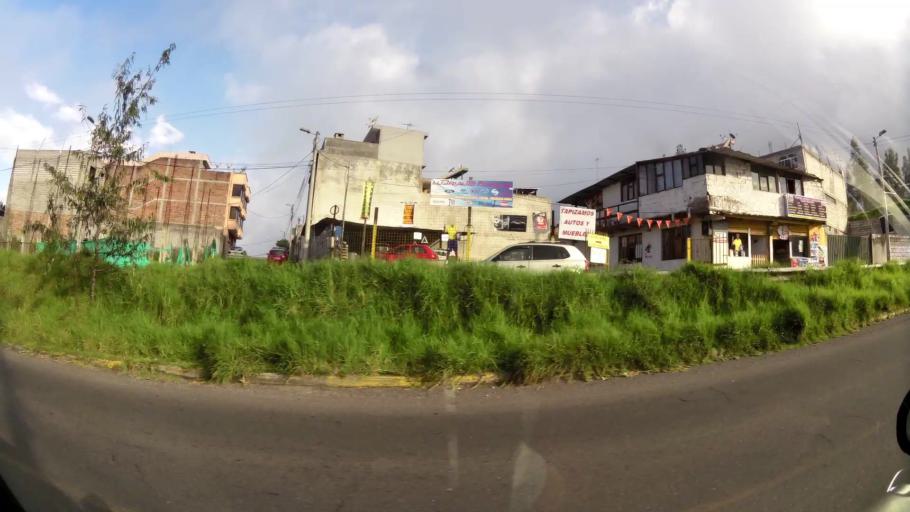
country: EC
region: Pichincha
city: Quito
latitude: -0.2565
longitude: -78.4960
